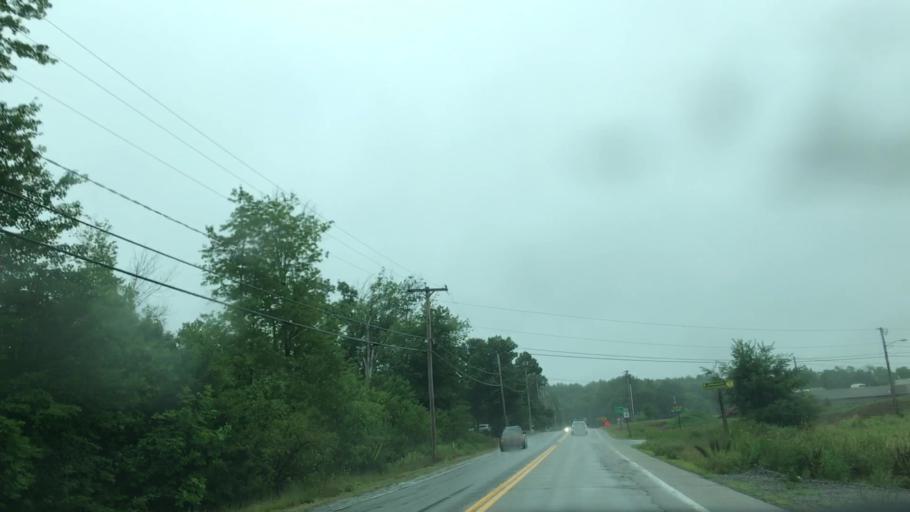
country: US
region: Maine
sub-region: York County
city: North Berwick
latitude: 43.2994
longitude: -70.7472
